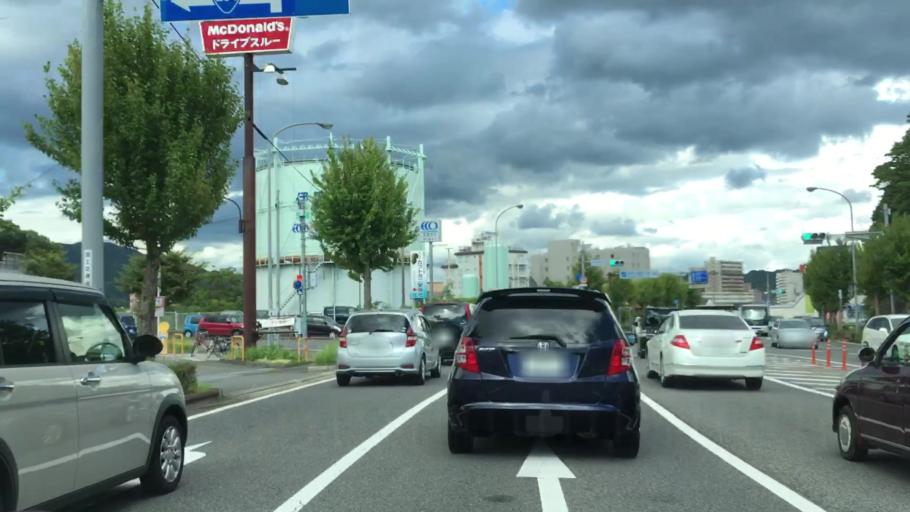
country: JP
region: Saga Prefecture
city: Imaricho-ko
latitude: 33.2692
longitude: 129.8684
